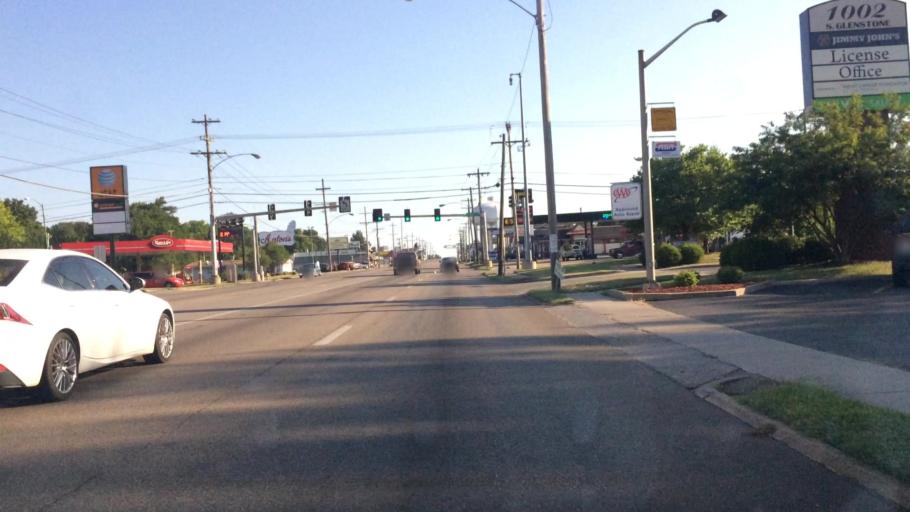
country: US
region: Missouri
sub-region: Greene County
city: Springfield
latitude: 37.1956
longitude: -93.2620
